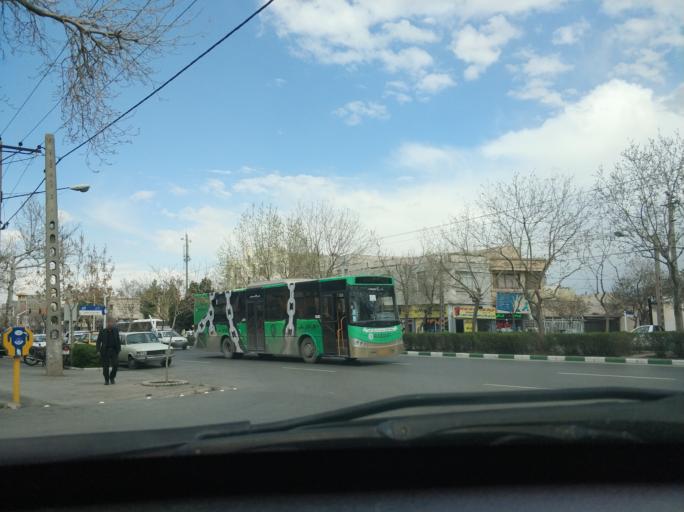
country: IR
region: Razavi Khorasan
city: Mashhad
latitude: 36.2665
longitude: 59.5865
